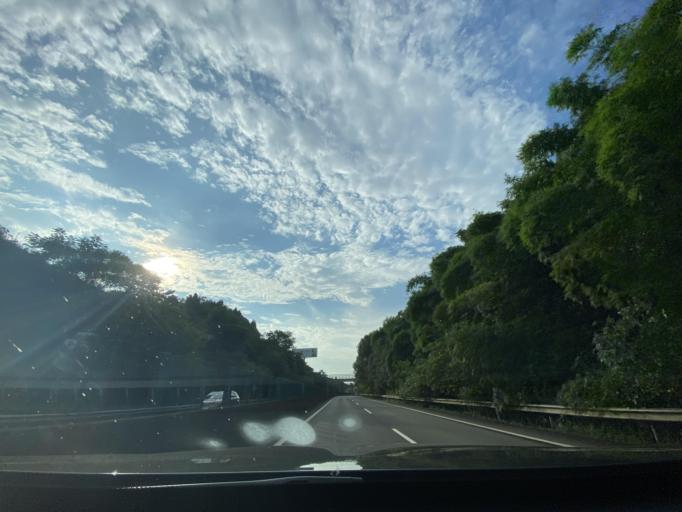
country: CN
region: Sichuan
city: Jiancheng
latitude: 30.2945
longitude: 104.5835
